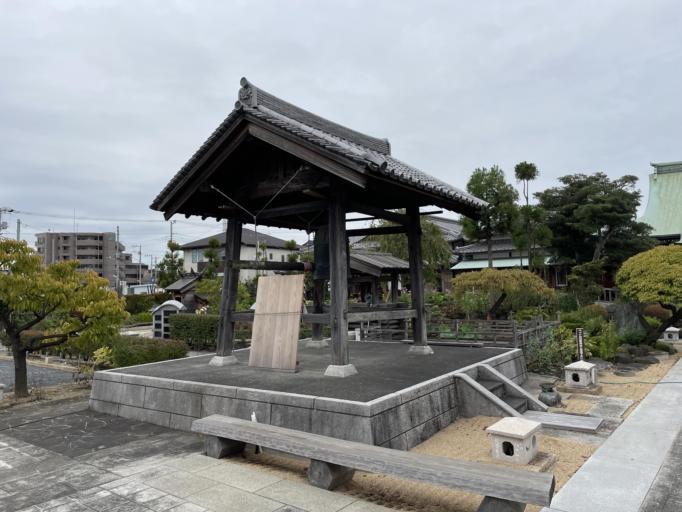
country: JP
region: Saitama
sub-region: Kawaguchi-shi
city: Hatogaya-honcho
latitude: 35.8073
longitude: 139.7649
